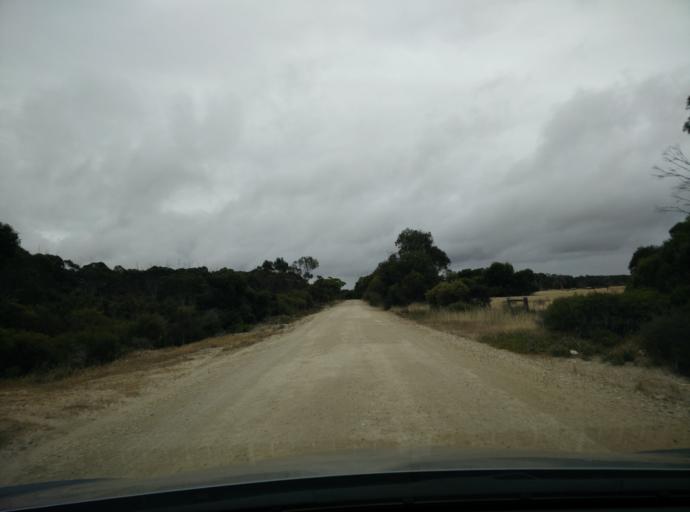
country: AU
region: South Australia
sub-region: Kangaroo Island
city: Kingscote
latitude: -35.8735
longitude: 137.4974
